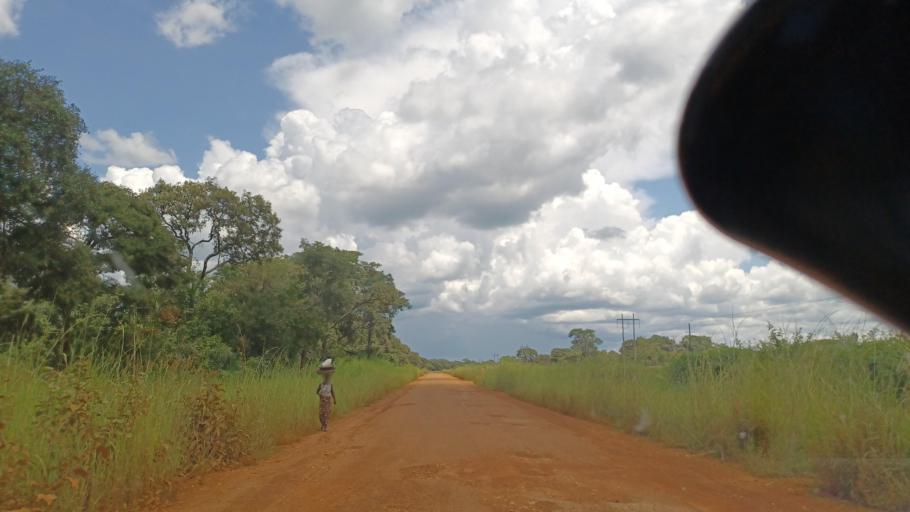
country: ZM
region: North-Western
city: Solwezi
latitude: -12.6890
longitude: 26.0404
